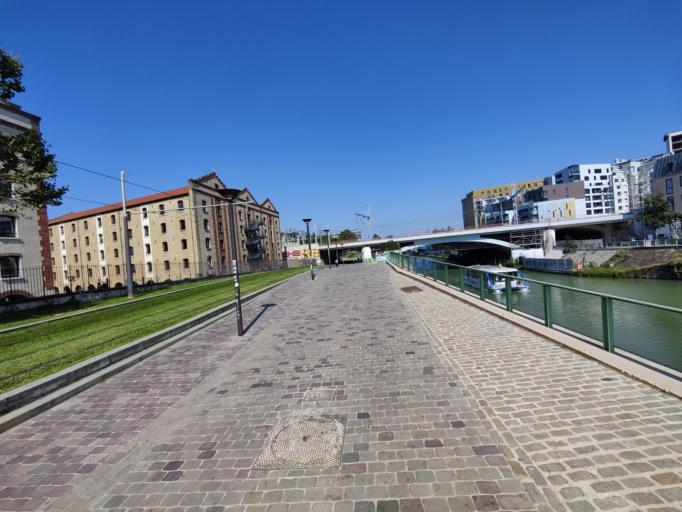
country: FR
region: Ile-de-France
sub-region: Departement de Seine-Saint-Denis
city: Aubervilliers
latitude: 48.8969
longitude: 2.3829
